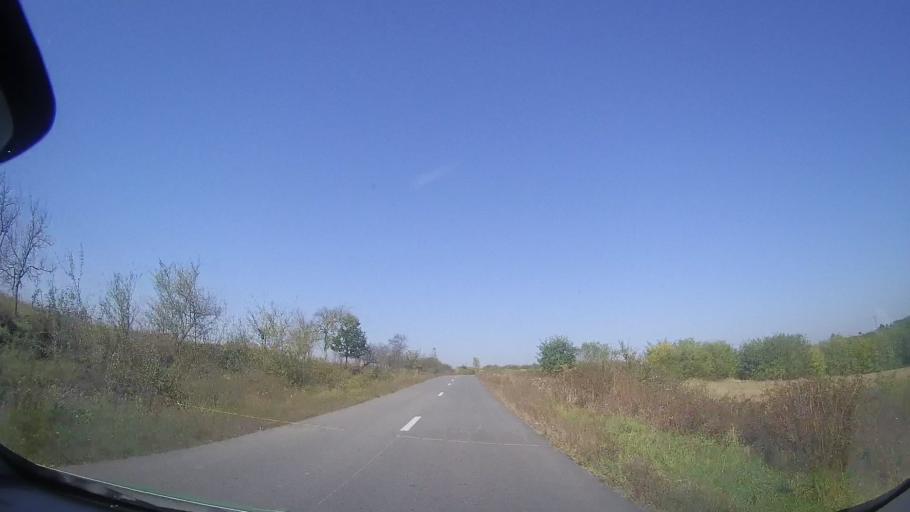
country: RO
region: Timis
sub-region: Comuna Balint
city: Balint
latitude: 45.8214
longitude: 21.8515
